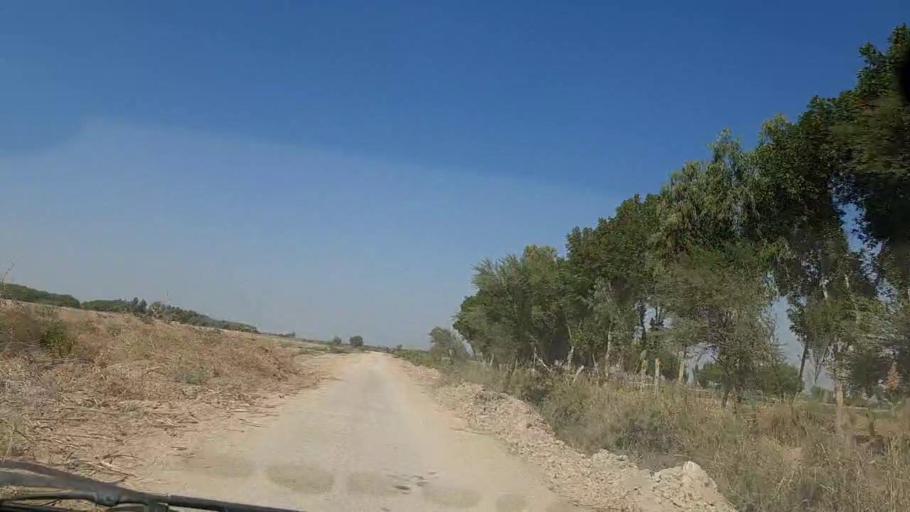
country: PK
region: Sindh
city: Mirwah Gorchani
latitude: 25.3900
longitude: 68.9716
